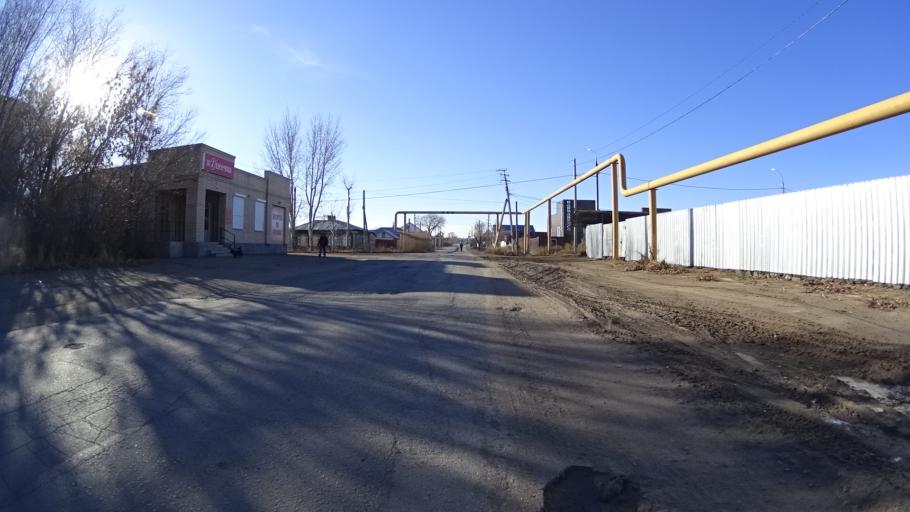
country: RU
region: Chelyabinsk
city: Troitsk
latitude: 54.0927
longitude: 61.5477
